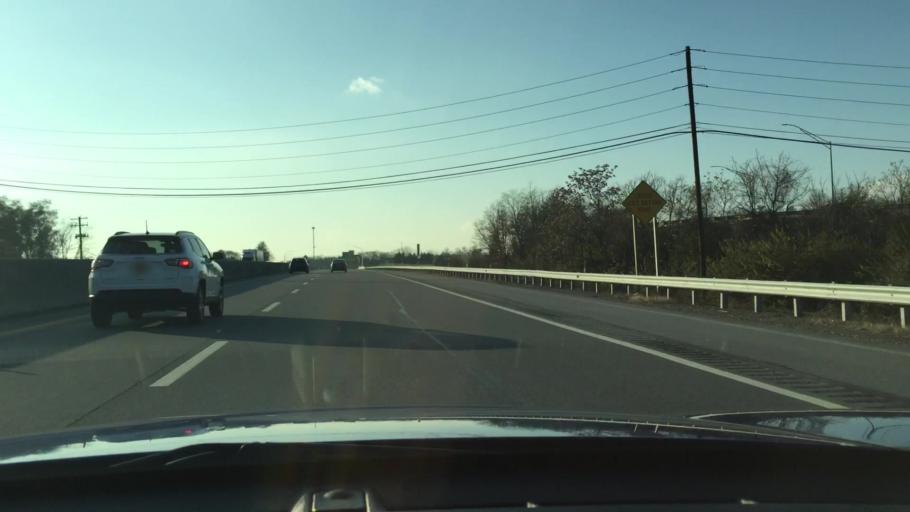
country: US
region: Pennsylvania
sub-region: Cumberland County
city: Schlusser
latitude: 40.2282
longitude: -77.1455
